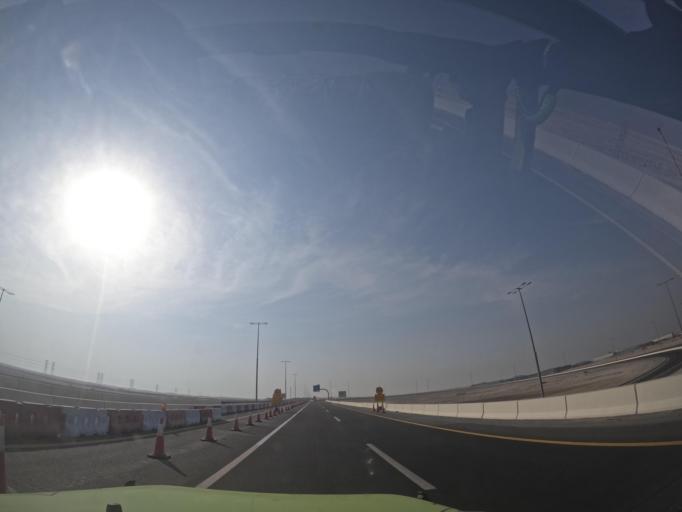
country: AE
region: Dubai
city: Dubai
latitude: 24.7926
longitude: 55.0766
